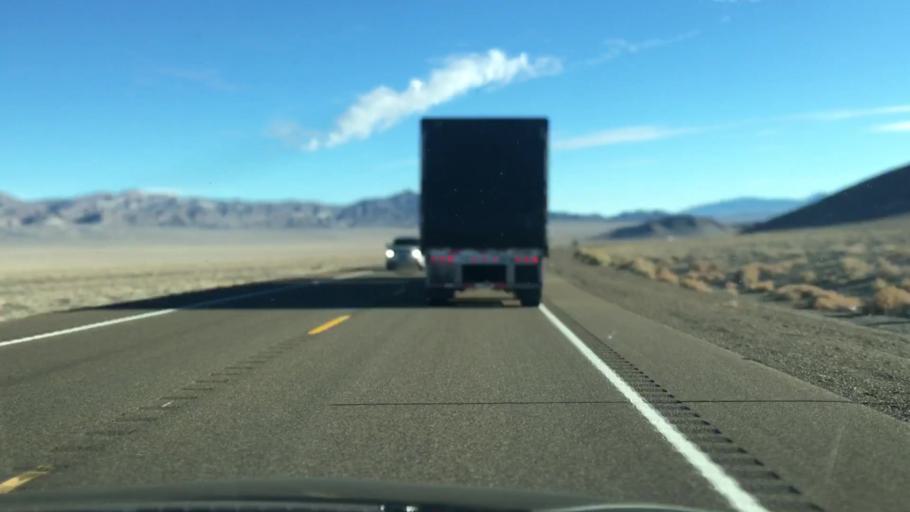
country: US
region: Nevada
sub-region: Nye County
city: Tonopah
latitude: 38.1727
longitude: -117.9588
